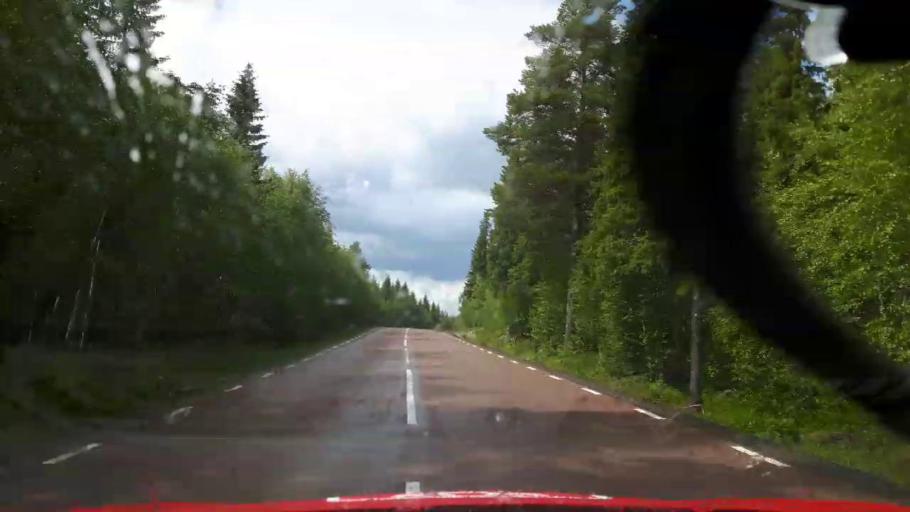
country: SE
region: Jaemtland
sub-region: Krokoms Kommun
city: Valla
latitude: 63.9637
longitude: 14.1762
